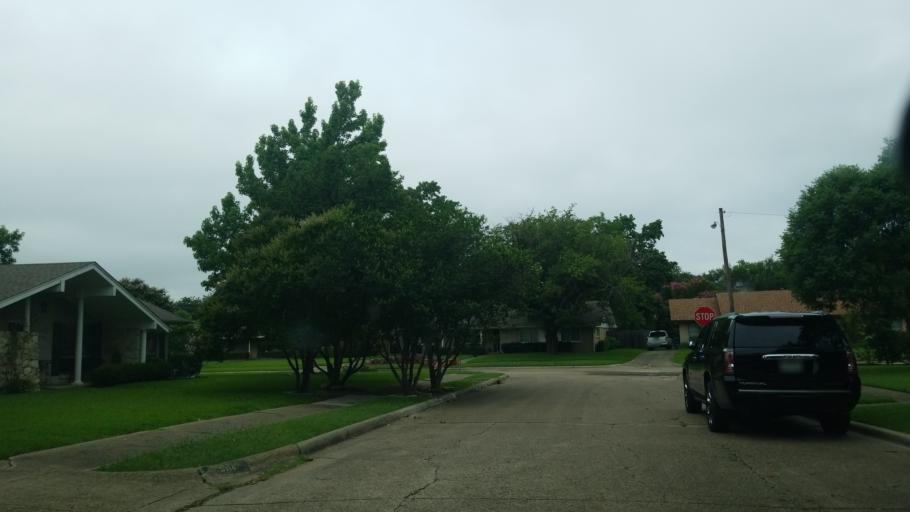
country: US
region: Texas
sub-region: Dallas County
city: Farmers Branch
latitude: 32.9009
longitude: -96.8707
